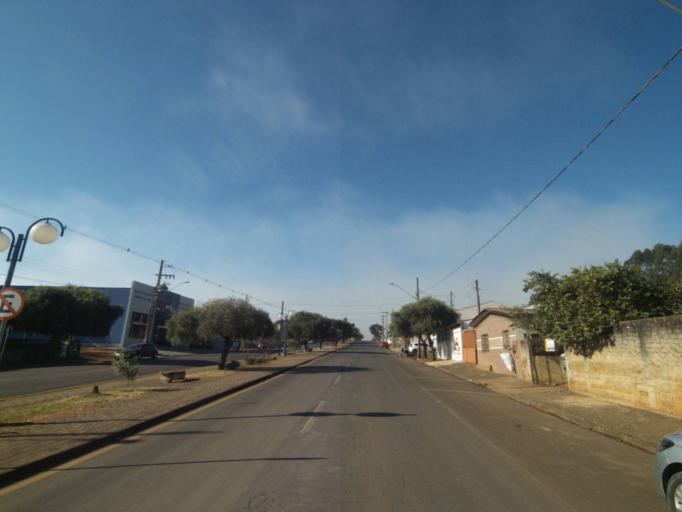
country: BR
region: Parana
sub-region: Tibagi
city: Tibagi
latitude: -24.5201
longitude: -50.4118
